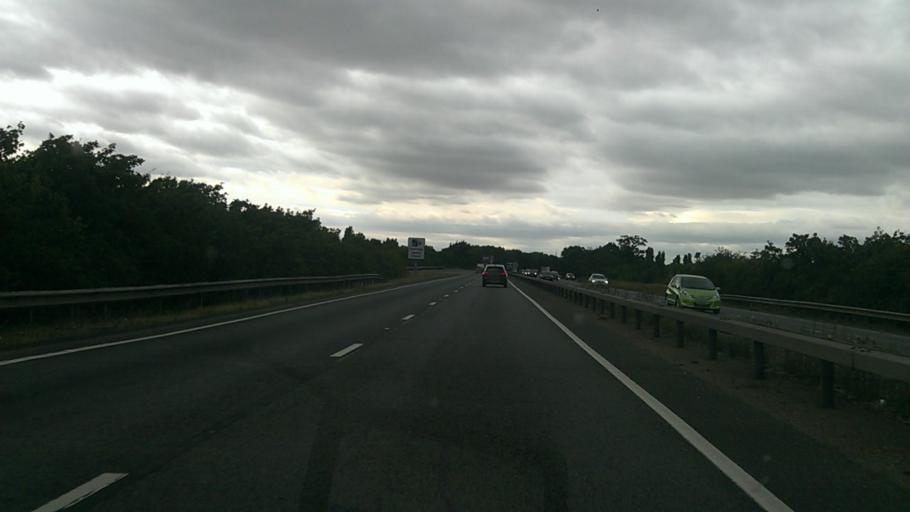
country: GB
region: England
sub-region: Cambridgeshire
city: Godmanchester
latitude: 52.3188
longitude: -0.1600
